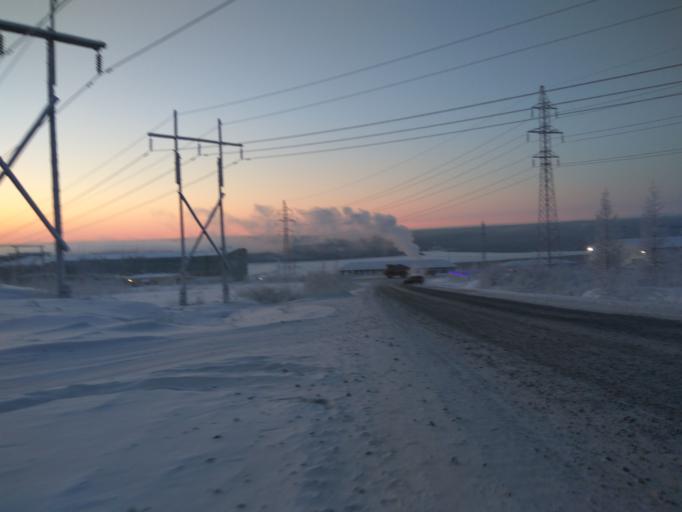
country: RU
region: Sakha
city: Aykhal
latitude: 65.9392
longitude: 111.5073
